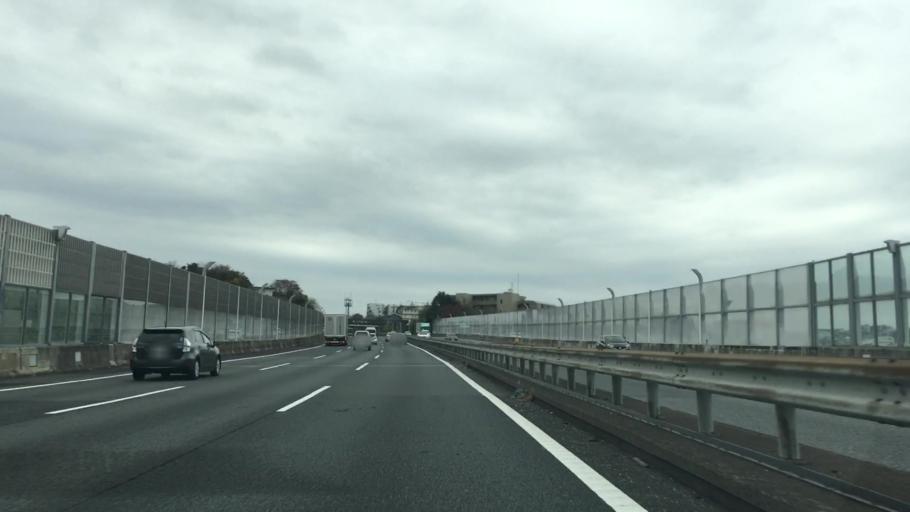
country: JP
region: Tokyo
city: Chofugaoka
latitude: 35.6104
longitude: 139.5870
